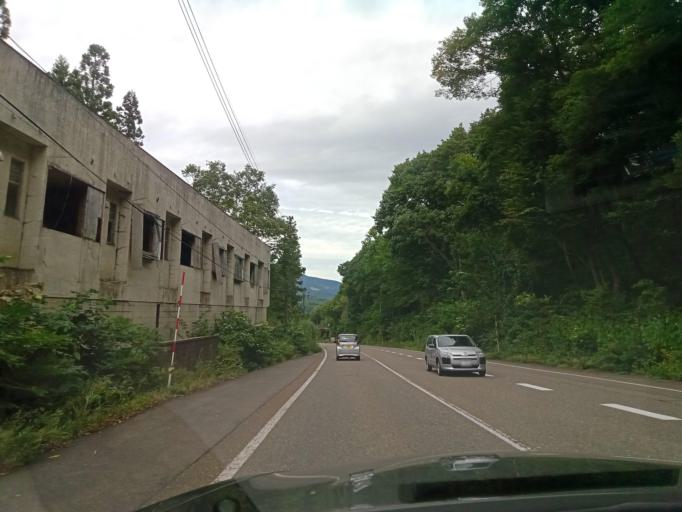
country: JP
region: Niigata
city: Arai
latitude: 36.8462
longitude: 138.1986
